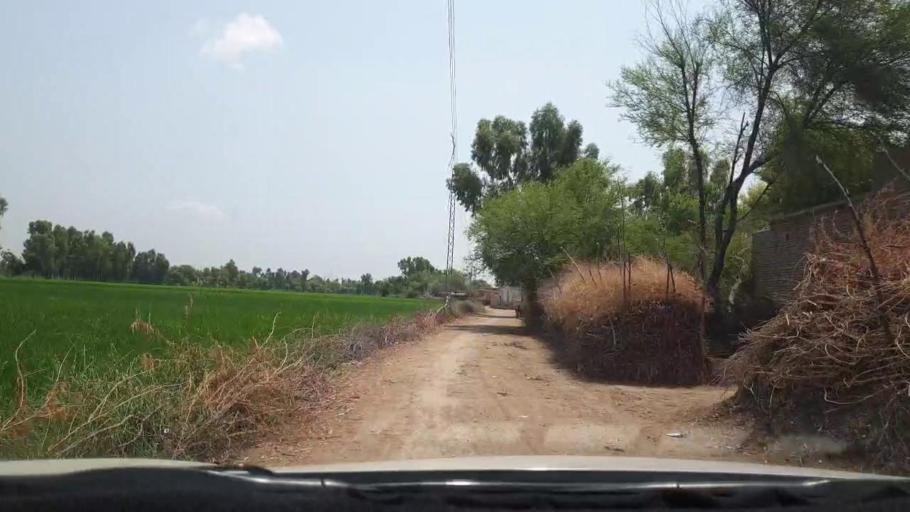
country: PK
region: Sindh
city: New Badah
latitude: 27.2970
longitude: 68.0711
